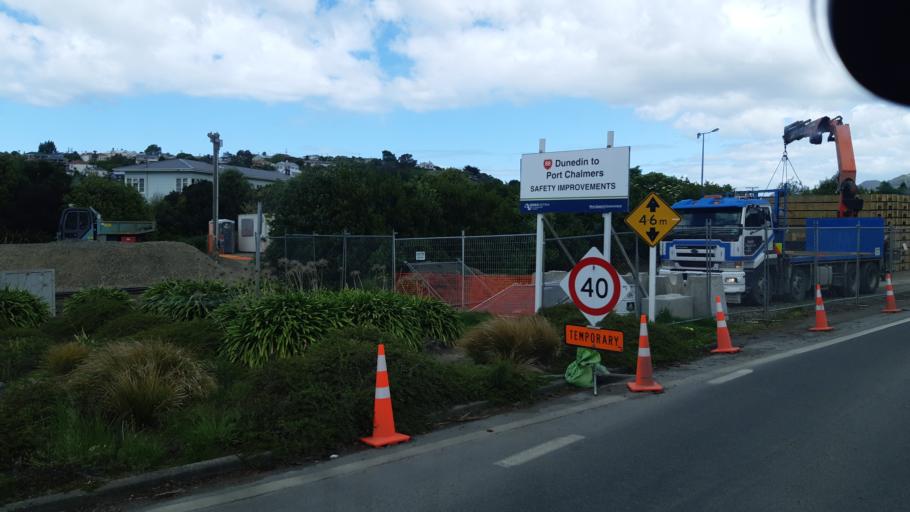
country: NZ
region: Otago
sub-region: Dunedin City
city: Portobello
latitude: -45.8178
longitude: 170.6188
